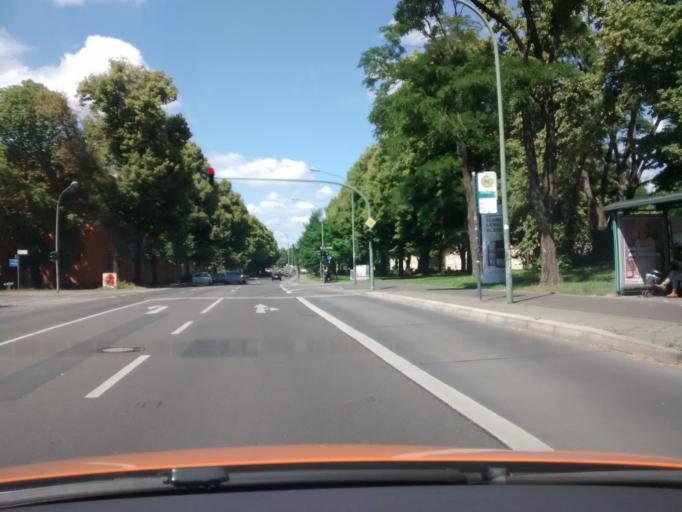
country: DE
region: Brandenburg
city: Potsdam
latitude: 52.4196
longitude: 13.0554
